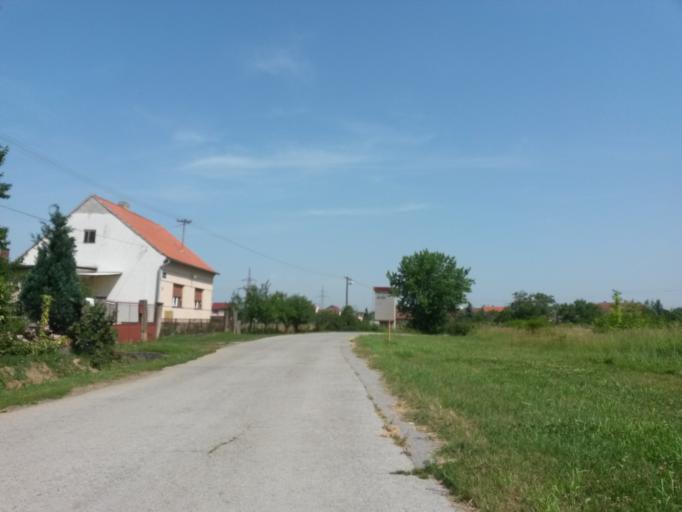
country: HR
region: Osjecko-Baranjska
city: Brijest
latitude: 45.5412
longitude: 18.6660
